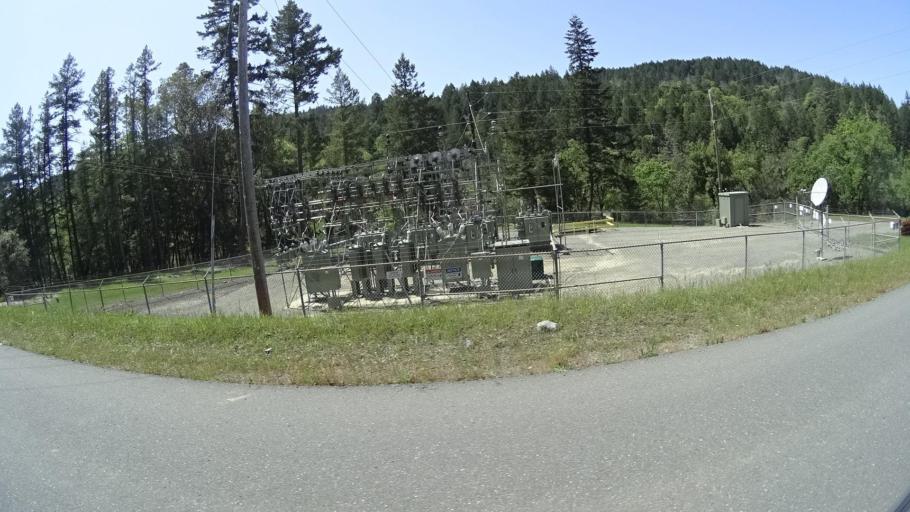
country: US
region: California
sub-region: Humboldt County
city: Redway
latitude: 40.2139
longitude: -123.5961
